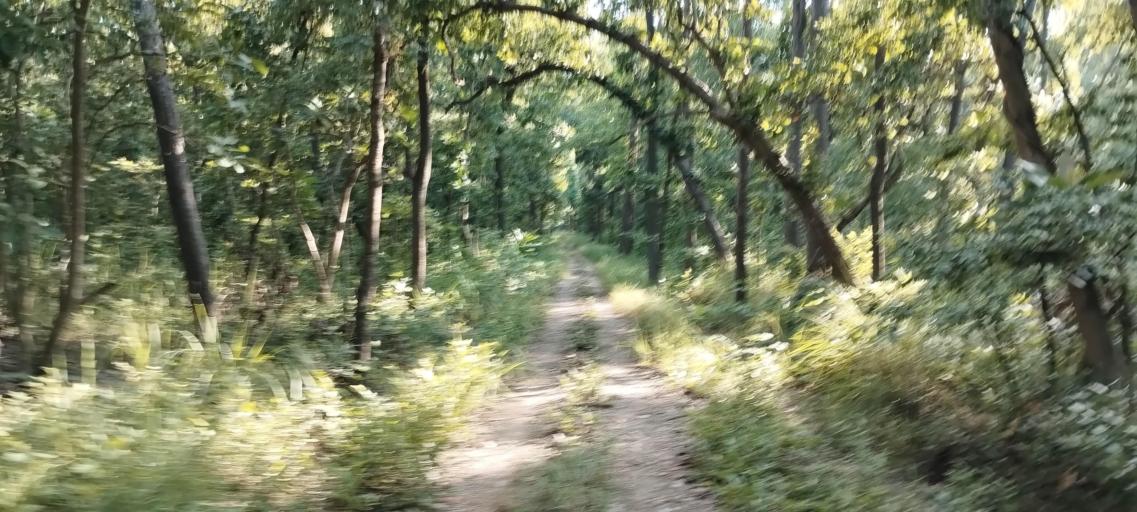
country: NP
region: Far Western
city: Tikapur
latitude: 28.5164
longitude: 81.2737
